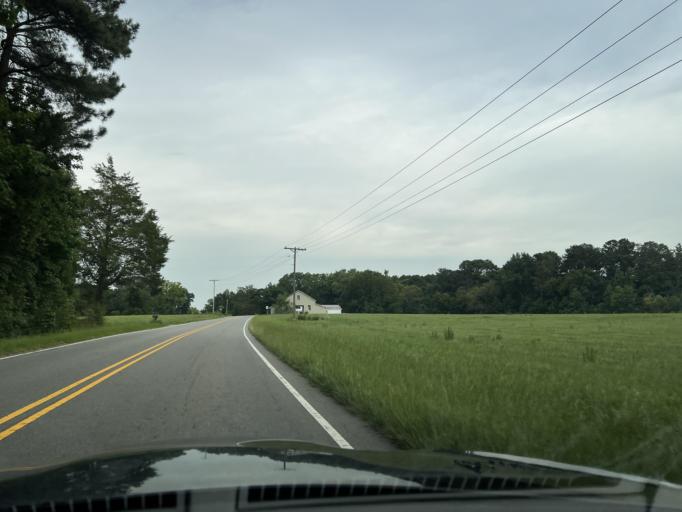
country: US
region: North Carolina
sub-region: Wake County
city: Wake Forest
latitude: 36.0123
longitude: -78.5587
